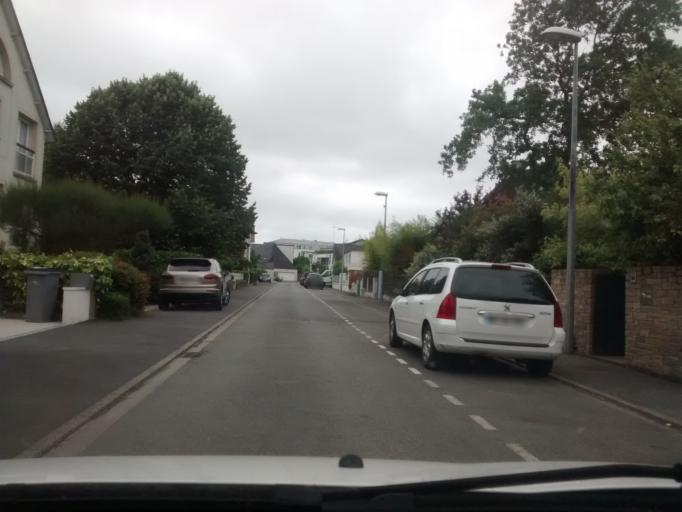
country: FR
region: Brittany
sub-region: Departement d'Ille-et-Vilaine
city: Cesson-Sevigne
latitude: 48.1133
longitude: -1.6135
